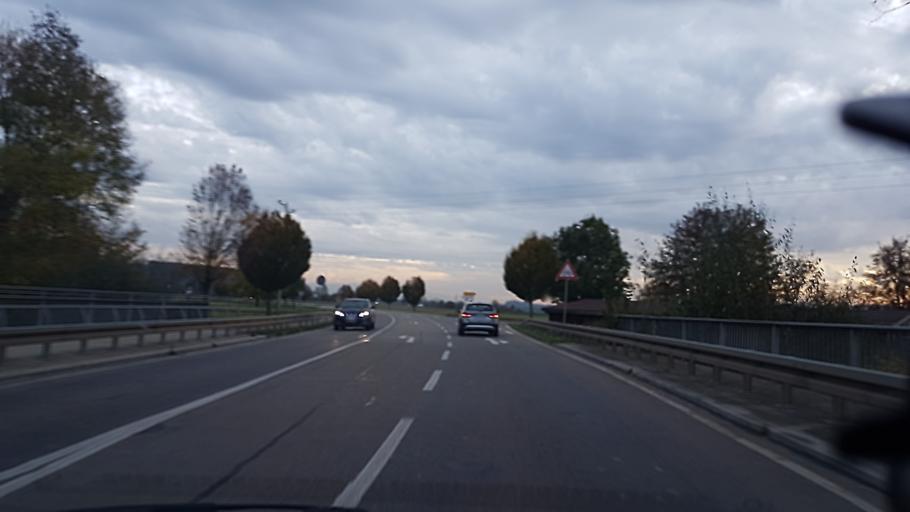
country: DE
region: Baden-Wuerttemberg
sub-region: Freiburg Region
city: Kenzingen
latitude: 48.1949
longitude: 7.7589
